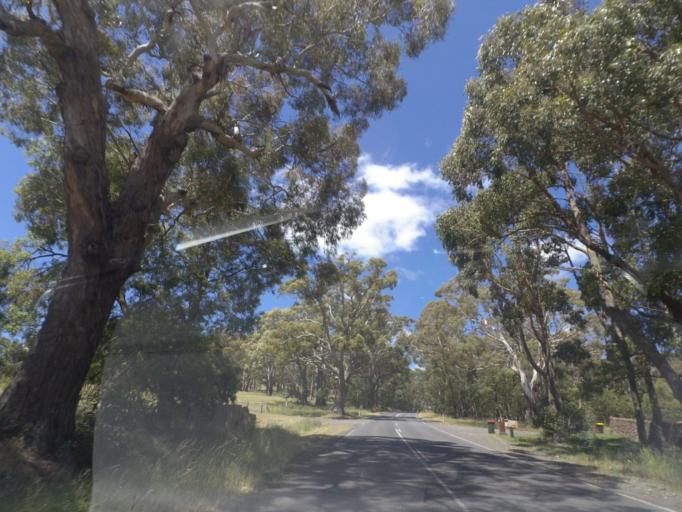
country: AU
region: Victoria
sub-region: Mount Alexander
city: Castlemaine
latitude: -37.2905
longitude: 144.2627
